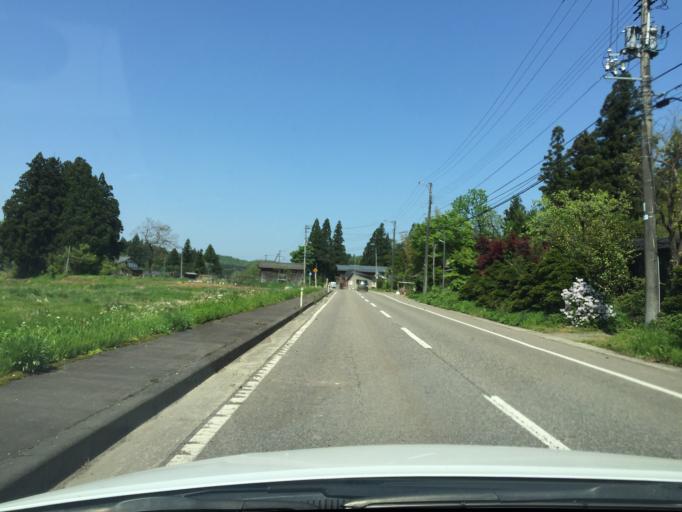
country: JP
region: Niigata
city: Kamo
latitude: 37.5760
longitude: 139.0859
